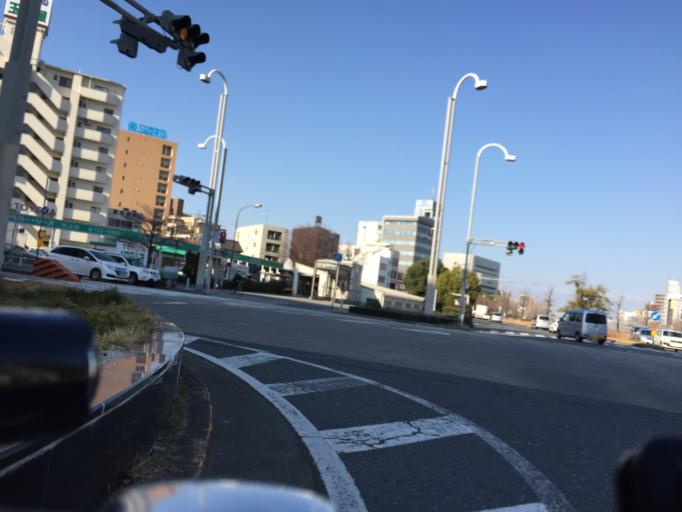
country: JP
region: Aichi
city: Nagoya-shi
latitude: 35.1592
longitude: 136.9355
